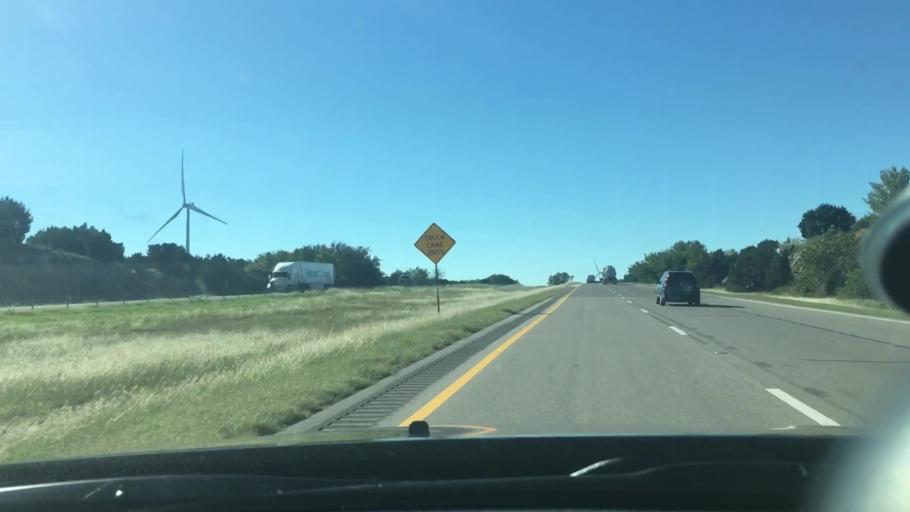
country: US
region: Oklahoma
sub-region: Murray County
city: Davis
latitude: 34.4087
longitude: -97.1395
